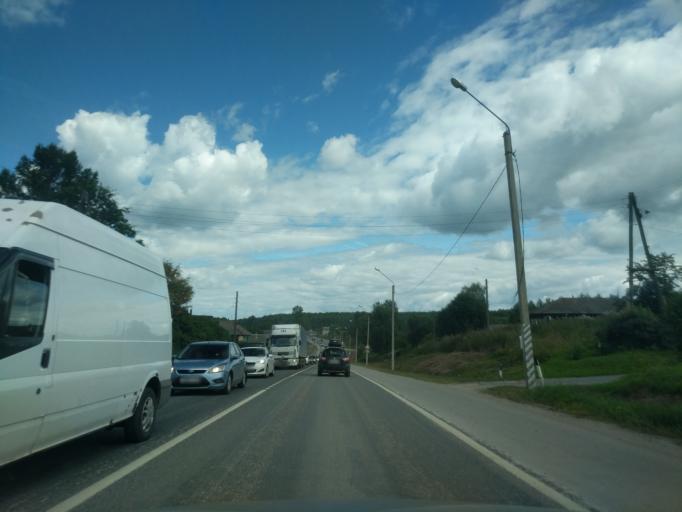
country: RU
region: Jaroslavl
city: Levashevo
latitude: 57.6537
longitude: 40.5586
